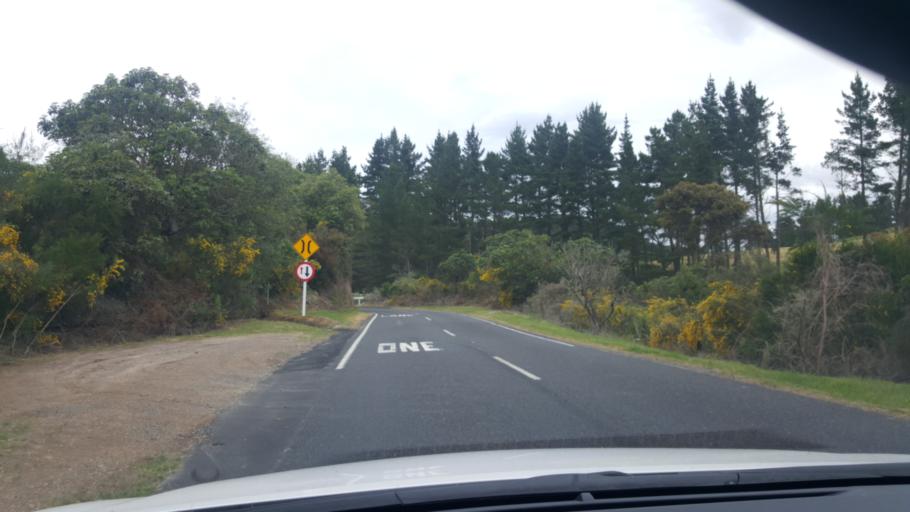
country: NZ
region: Bay of Plenty
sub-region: Rotorua District
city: Rotorua
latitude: -38.3553
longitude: 176.3625
